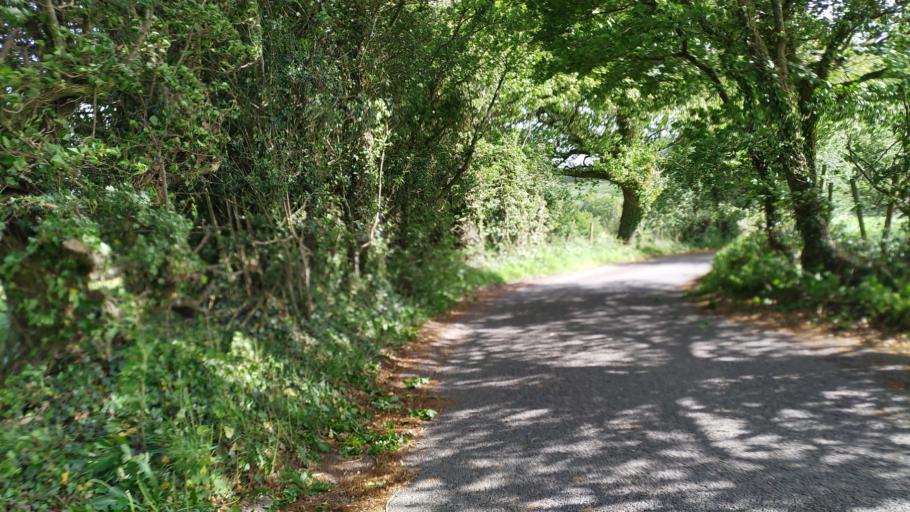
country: GB
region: England
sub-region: Lancashire
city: Chorley
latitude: 53.6439
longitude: -2.5976
